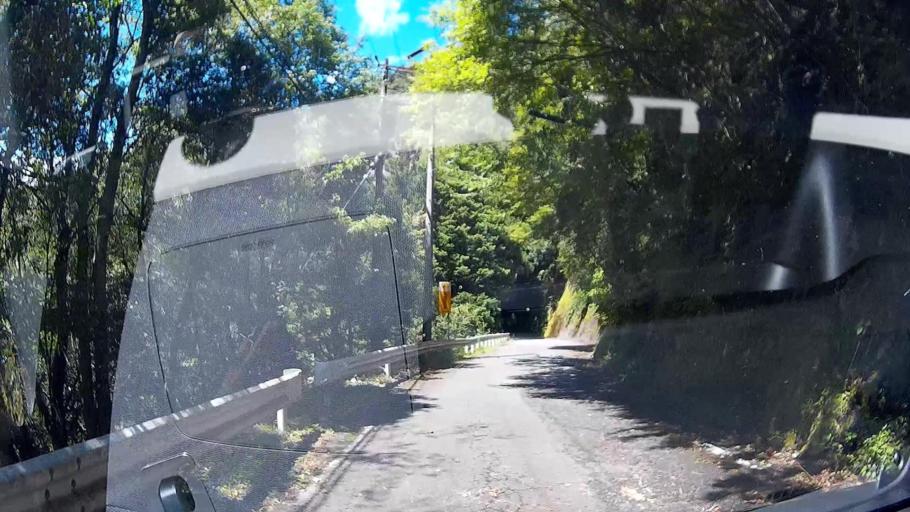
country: JP
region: Shizuoka
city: Shizuoka-shi
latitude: 35.1769
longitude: 138.2950
